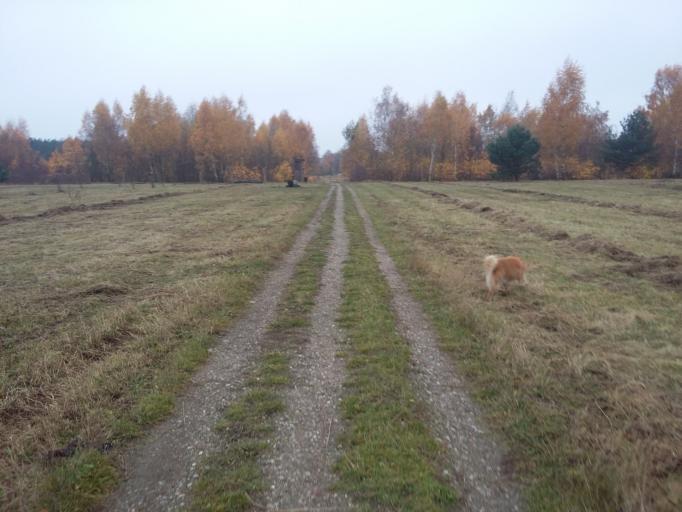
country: PL
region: Lodz Voivodeship
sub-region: Powiat pabianicki
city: Ksawerow
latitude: 51.7311
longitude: 19.3846
